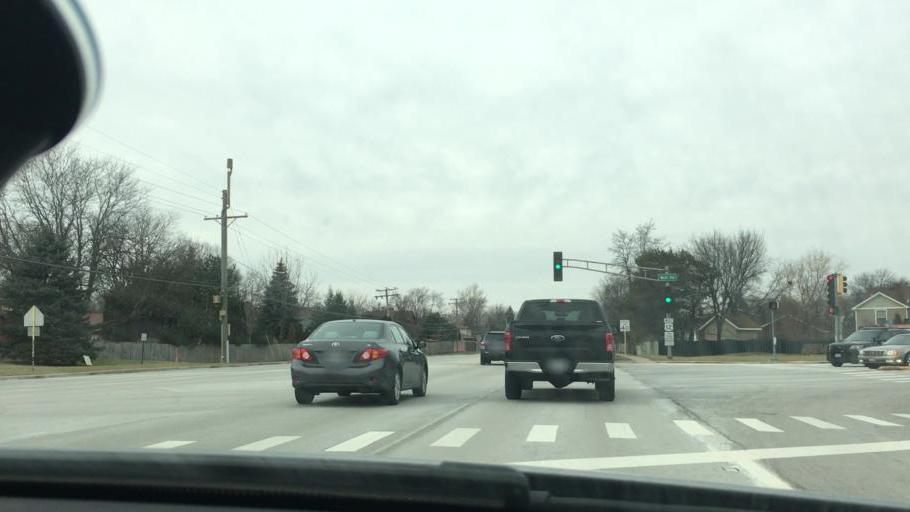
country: US
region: Illinois
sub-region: Cook County
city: Mount Prospect
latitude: 42.0608
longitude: -87.9100
